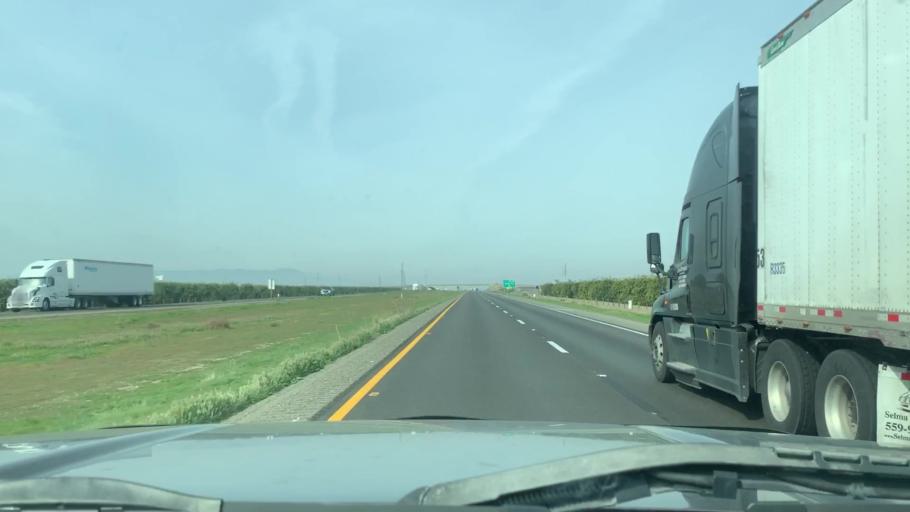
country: US
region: California
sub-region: Fresno County
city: Huron
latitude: 36.1316
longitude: -120.1530
